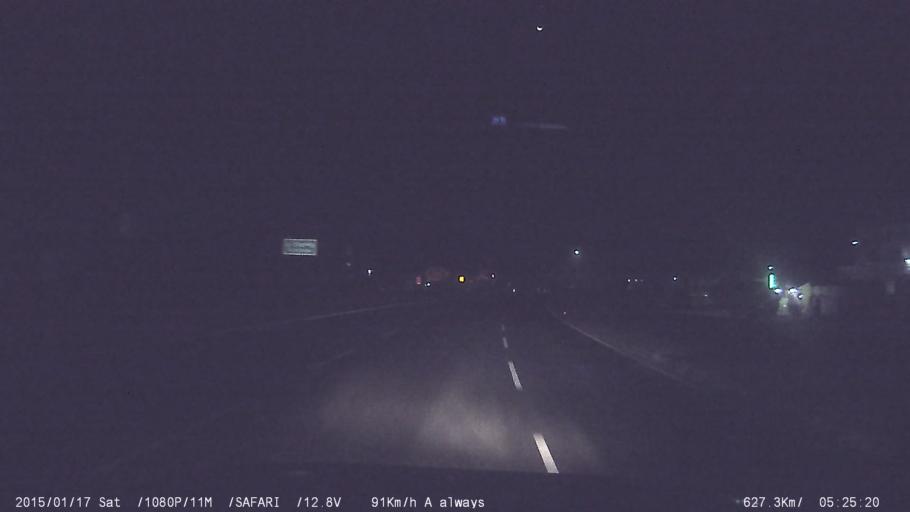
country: IN
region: Tamil Nadu
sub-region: Vellore
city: Katpadi
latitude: 12.9437
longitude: 79.2322
